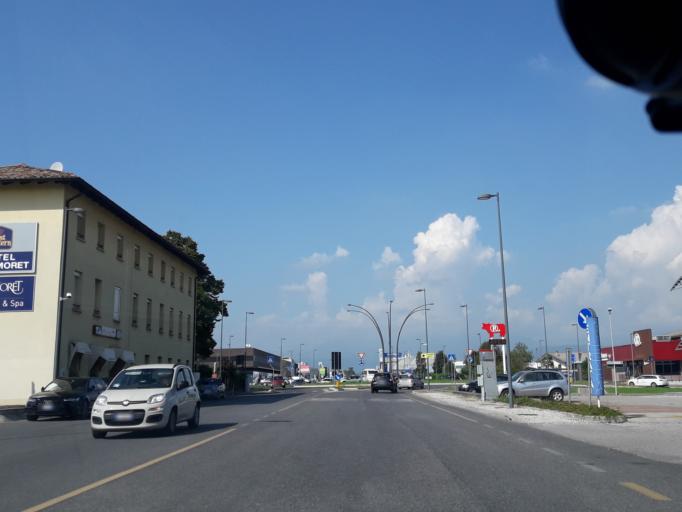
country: IT
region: Friuli Venezia Giulia
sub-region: Provincia di Udine
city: Feletto Umberto
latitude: 46.0974
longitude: 13.2307
